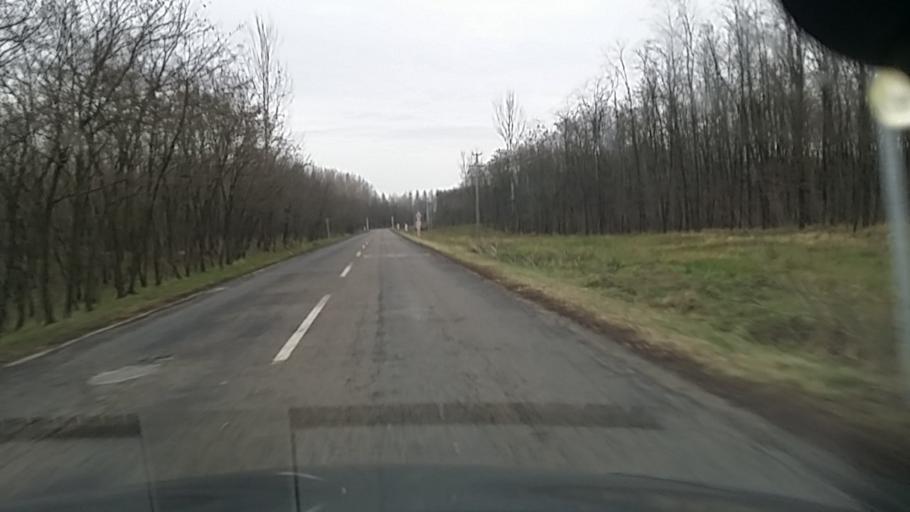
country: HU
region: Szabolcs-Szatmar-Bereg
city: Nyirbogdany
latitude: 48.0833
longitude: 21.8632
